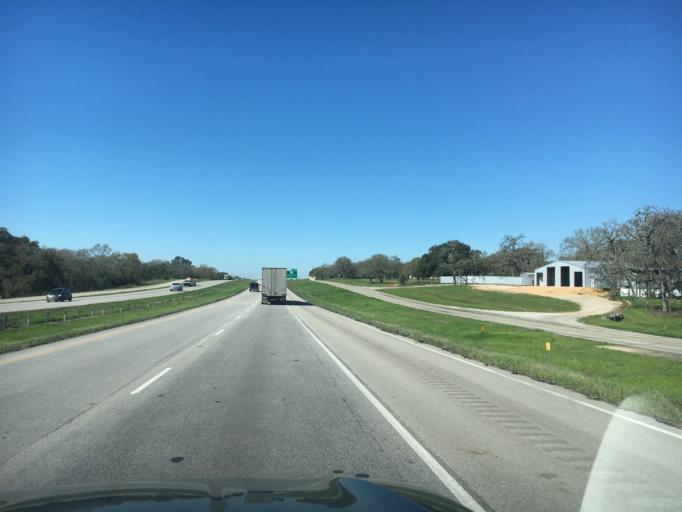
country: US
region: Texas
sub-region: Colorado County
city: Columbus
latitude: 29.7171
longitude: -96.4605
